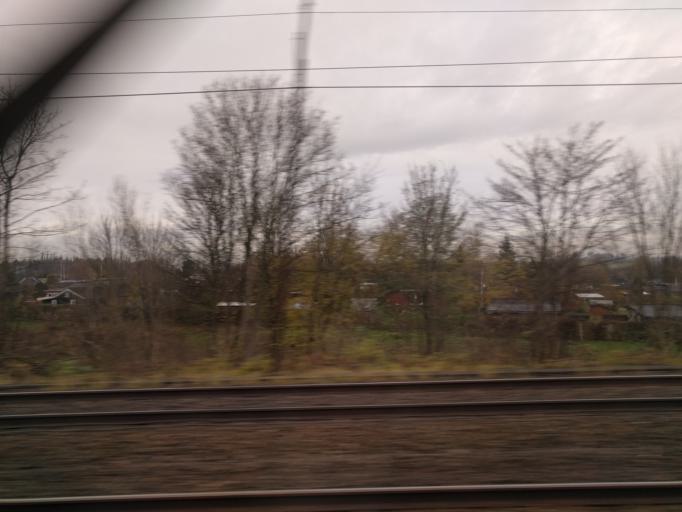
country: DK
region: Zealand
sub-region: Roskilde Kommune
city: Vindinge
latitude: 55.6489
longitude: 12.1504
